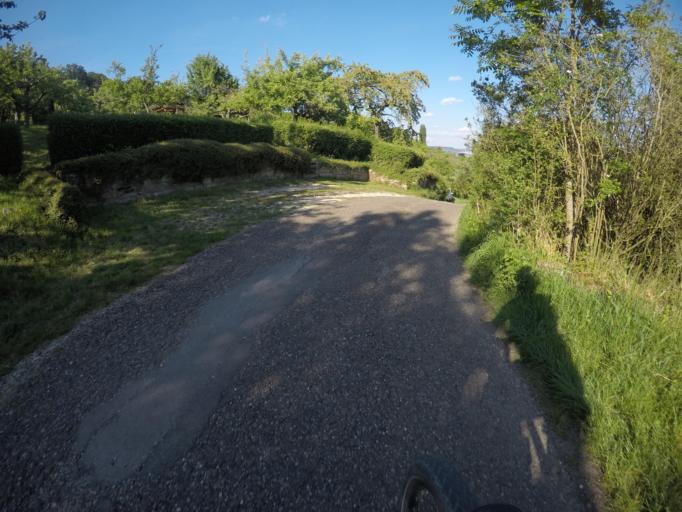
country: DE
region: Baden-Wuerttemberg
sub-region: Regierungsbezirk Stuttgart
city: Ostfildern
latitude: 48.7393
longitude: 9.2591
